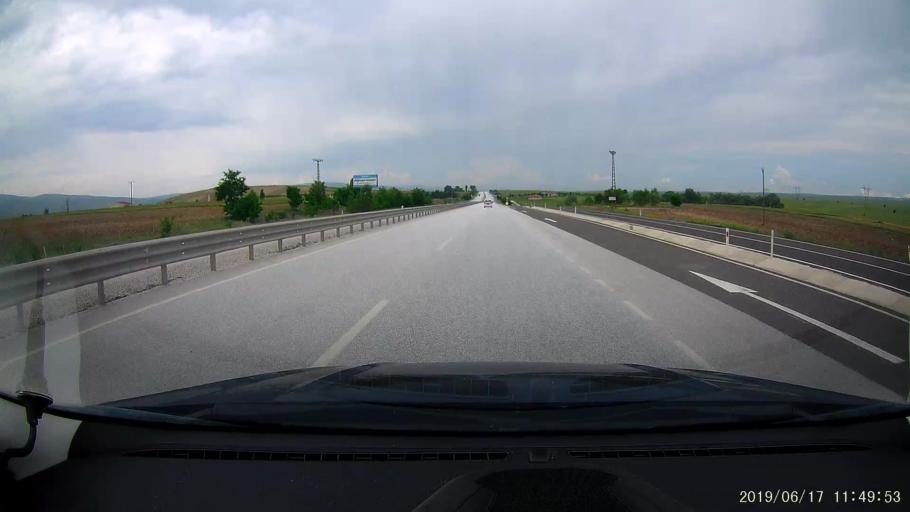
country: TR
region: Cankiri
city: Atkaracalar
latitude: 40.8338
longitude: 33.1456
